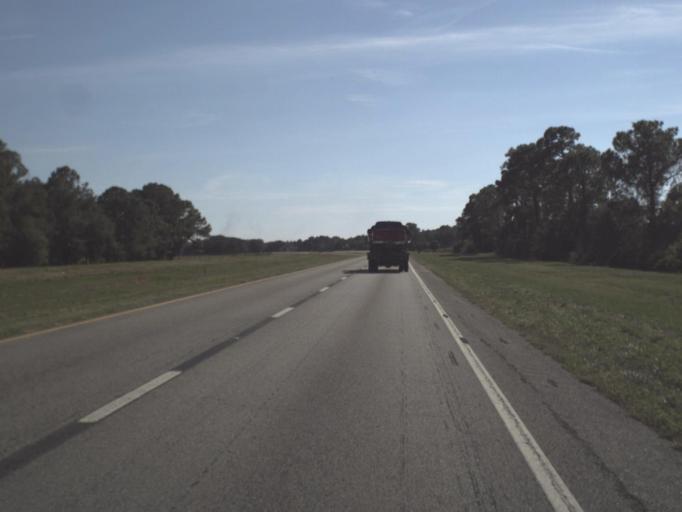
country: US
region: Florida
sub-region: Highlands County
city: Placid Lakes
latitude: 27.0382
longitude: -81.3421
